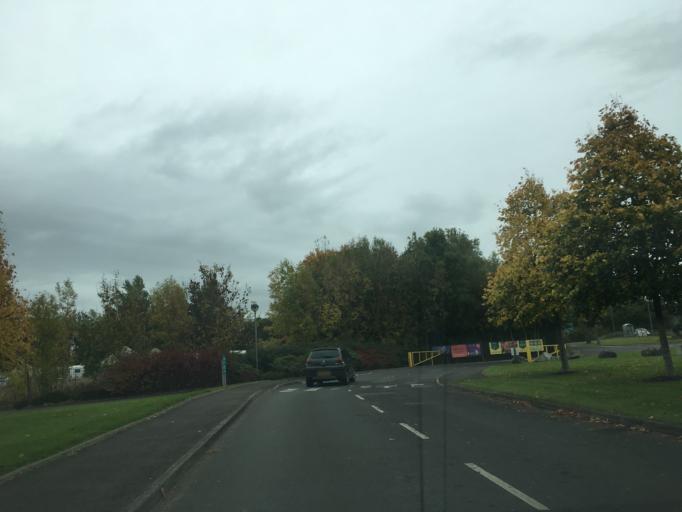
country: GB
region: Scotland
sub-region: Stirling
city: Bridge of Allan
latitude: 56.1378
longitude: -3.9793
